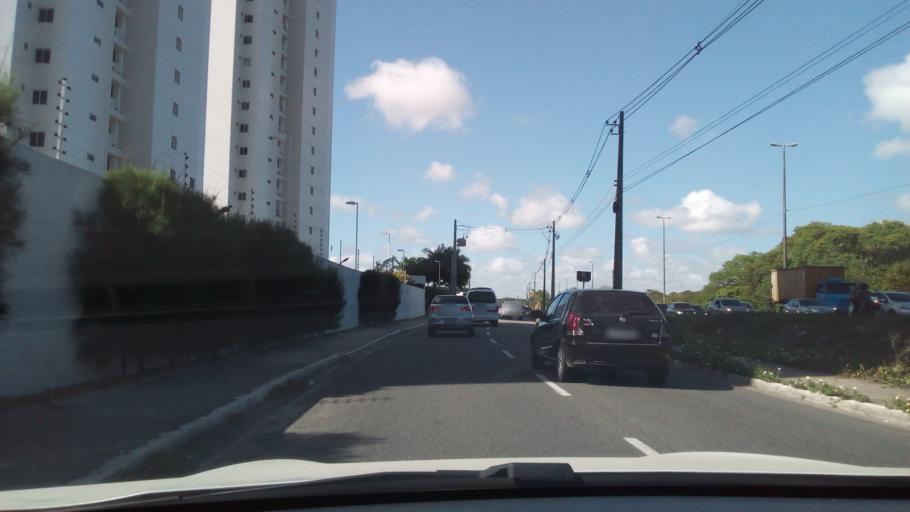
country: BR
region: Paraiba
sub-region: Joao Pessoa
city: Joao Pessoa
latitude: -7.1489
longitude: -34.8509
